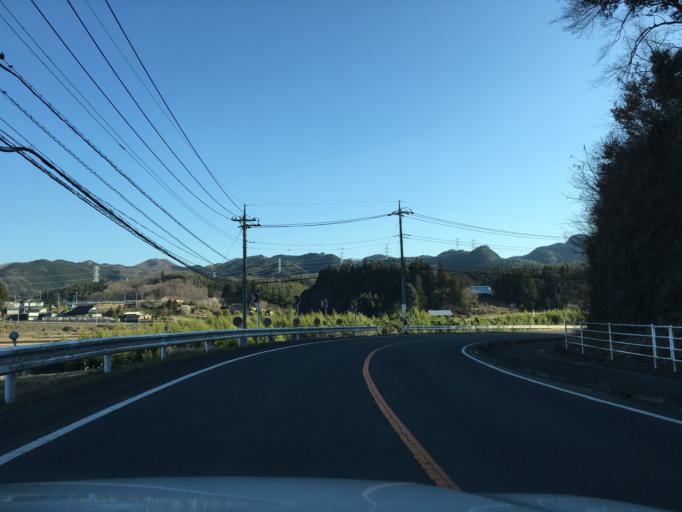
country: JP
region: Ibaraki
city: Daigo
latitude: 36.7799
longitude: 140.3061
